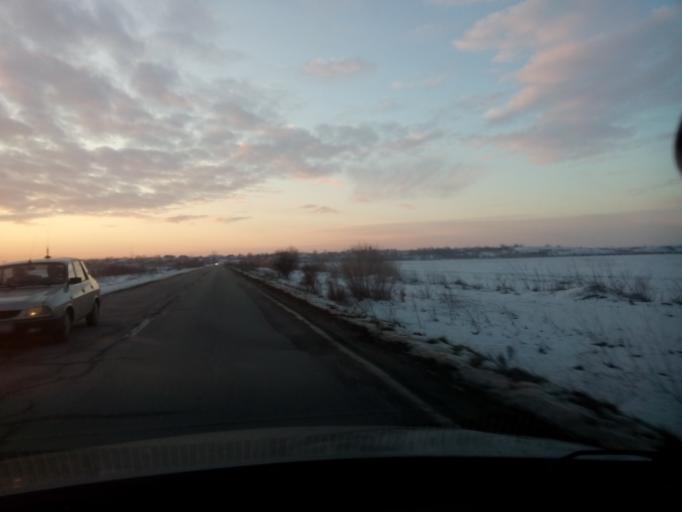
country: RO
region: Calarasi
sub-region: Comuna Budesti
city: Budesti
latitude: 44.2303
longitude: 26.4292
